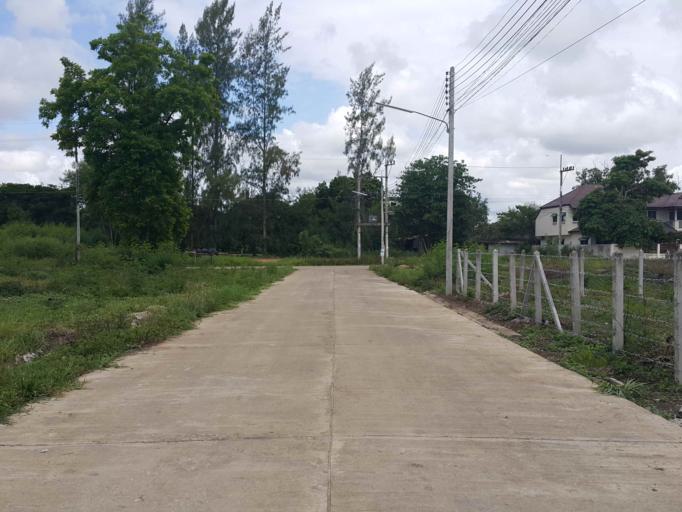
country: TH
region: Chiang Mai
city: Saraphi
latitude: 18.7210
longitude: 99.0479
